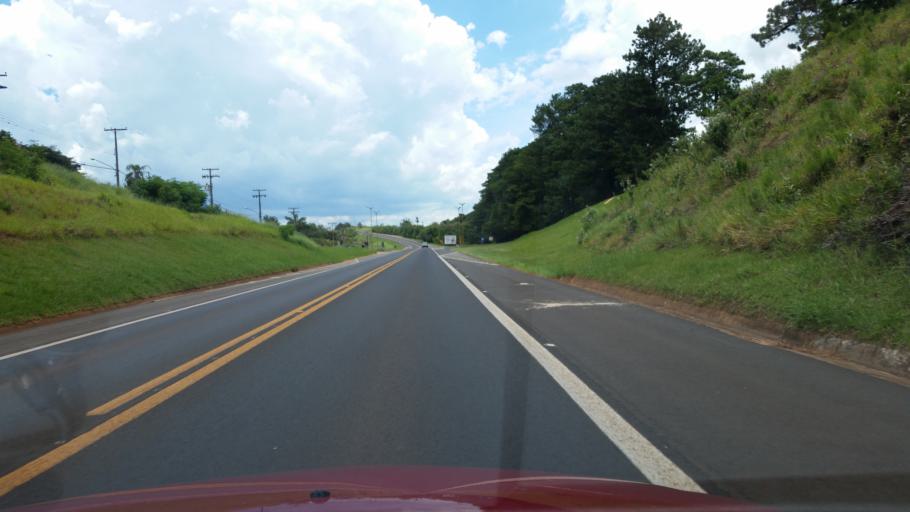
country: BR
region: Sao Paulo
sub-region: Itai
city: Itai
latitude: -23.2768
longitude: -49.0217
